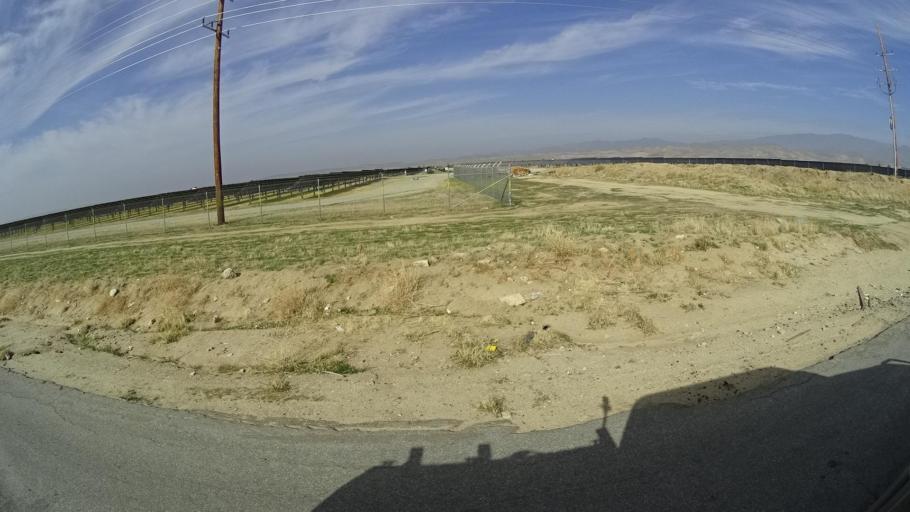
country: US
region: California
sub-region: Kern County
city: Arvin
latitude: 35.3256
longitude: -118.8169
